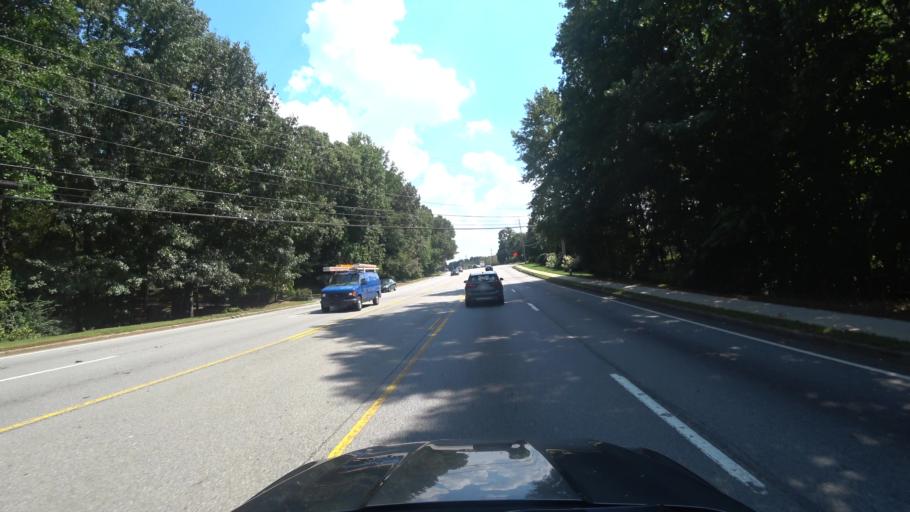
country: US
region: Georgia
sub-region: Gwinnett County
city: Norcross
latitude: 33.9570
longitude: -84.2453
